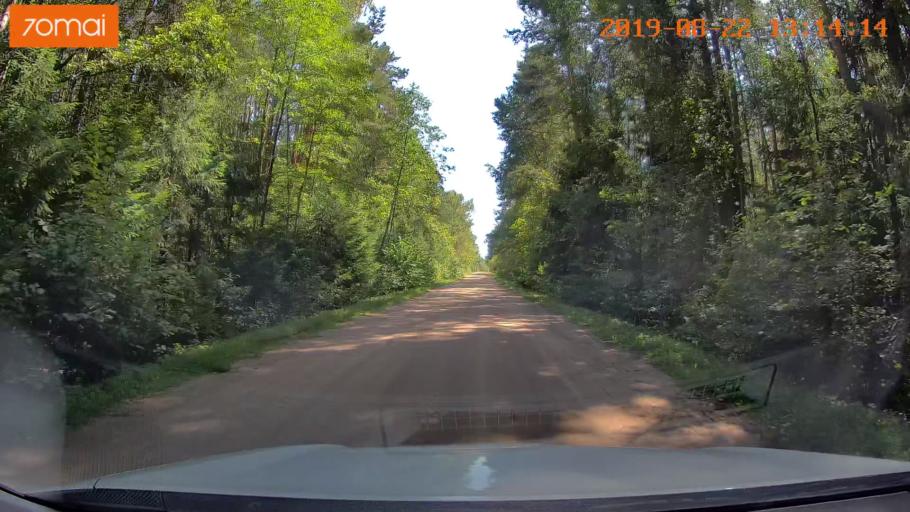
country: BY
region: Minsk
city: Prawdzinski
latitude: 53.2697
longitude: 27.8849
